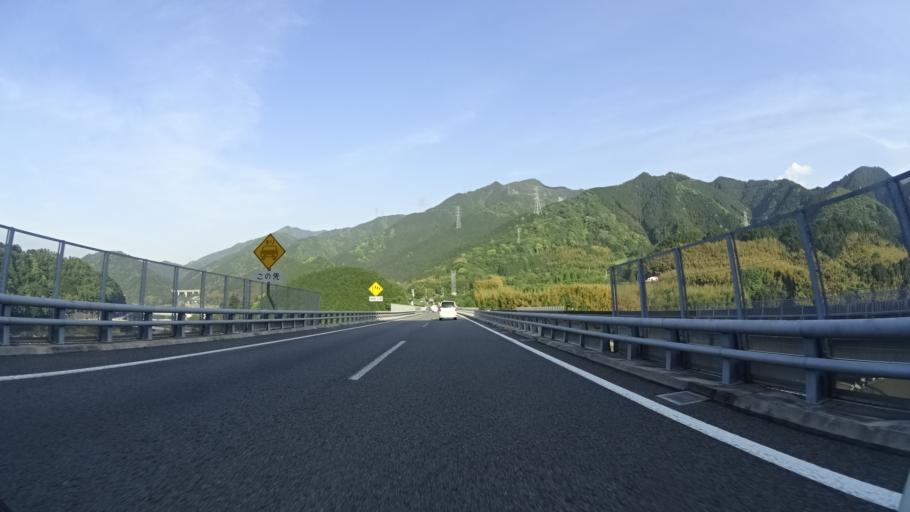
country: JP
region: Ehime
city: Saijo
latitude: 33.8861
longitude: 133.1787
